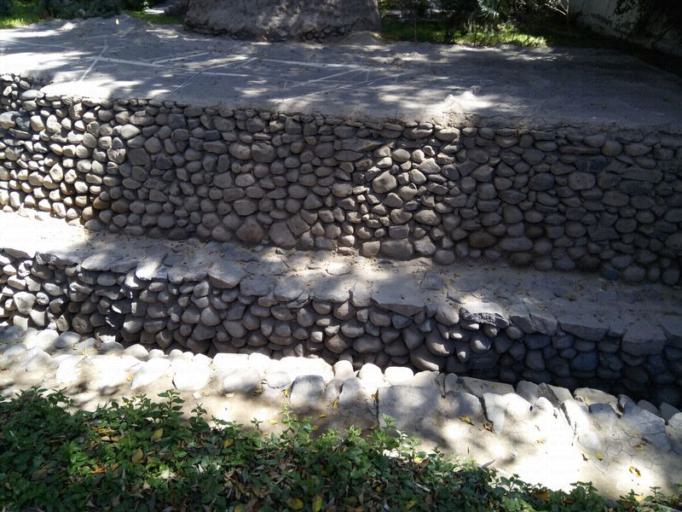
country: PE
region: Ica
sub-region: Provincia de Nazca
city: Nazca
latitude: -14.8256
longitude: -74.9293
